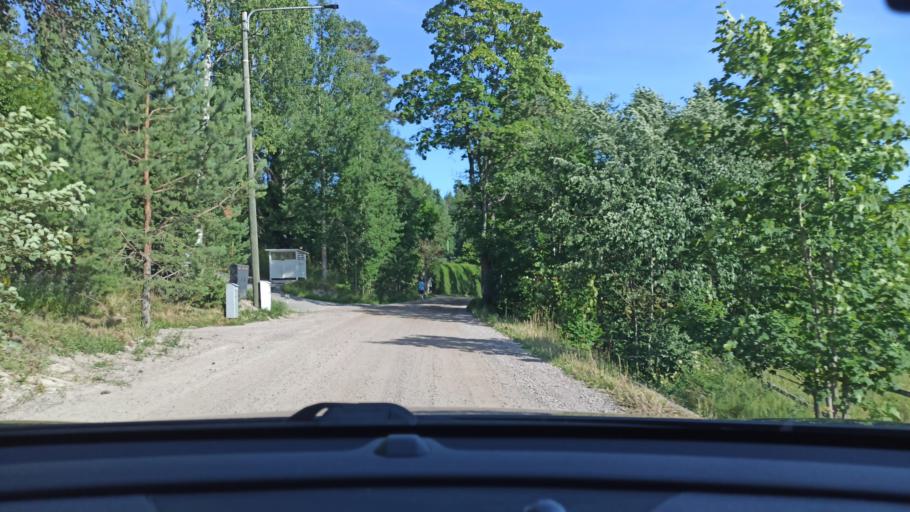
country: FI
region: Uusimaa
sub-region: Helsinki
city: Espoo
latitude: 60.2100
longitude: 24.5532
